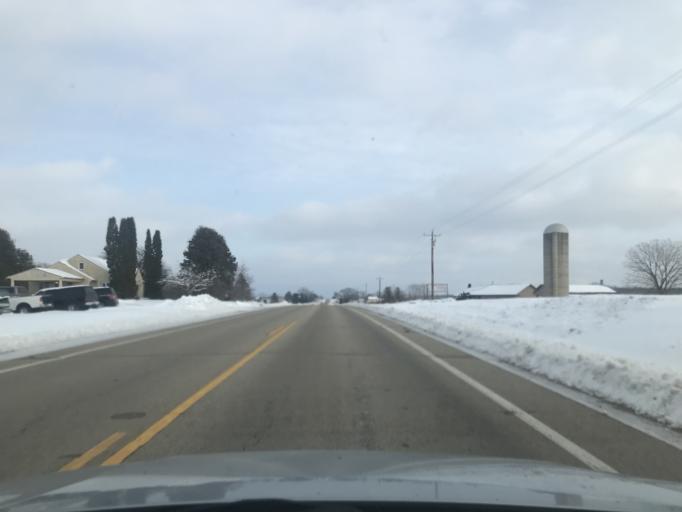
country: US
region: Wisconsin
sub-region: Oconto County
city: Oconto
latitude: 44.8932
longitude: -87.9862
